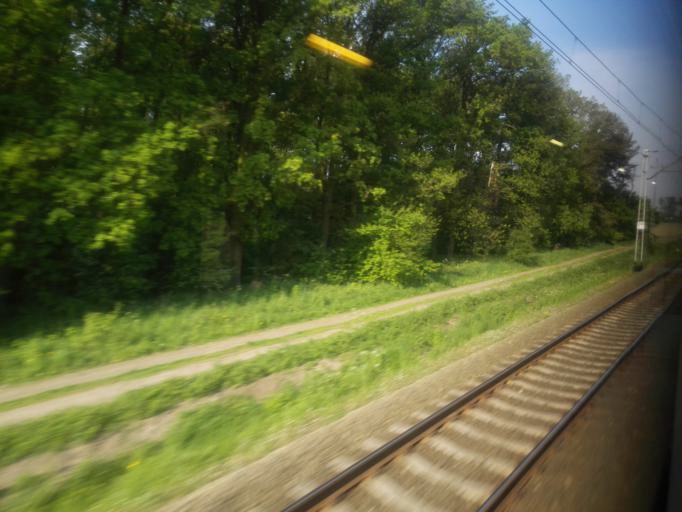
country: PL
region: Greater Poland Voivodeship
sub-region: Powiat wrzesinski
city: Wrzesnia
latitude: 52.3348
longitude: 17.6203
